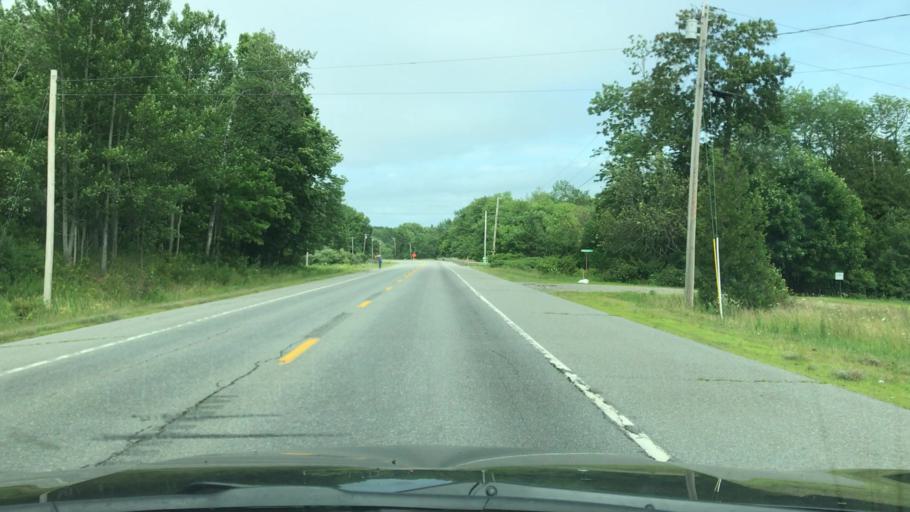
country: US
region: Maine
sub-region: Waldo County
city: Stockton Springs
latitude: 44.4961
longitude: -68.8374
